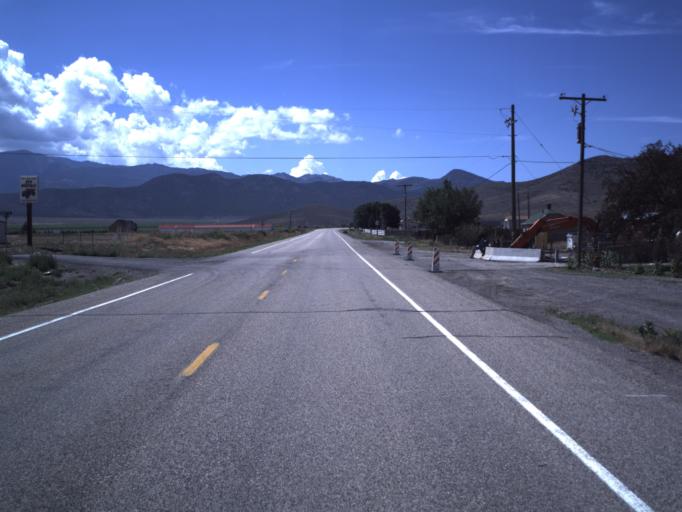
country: US
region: Utah
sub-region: Piute County
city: Junction
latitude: 38.1649
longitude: -112.2796
